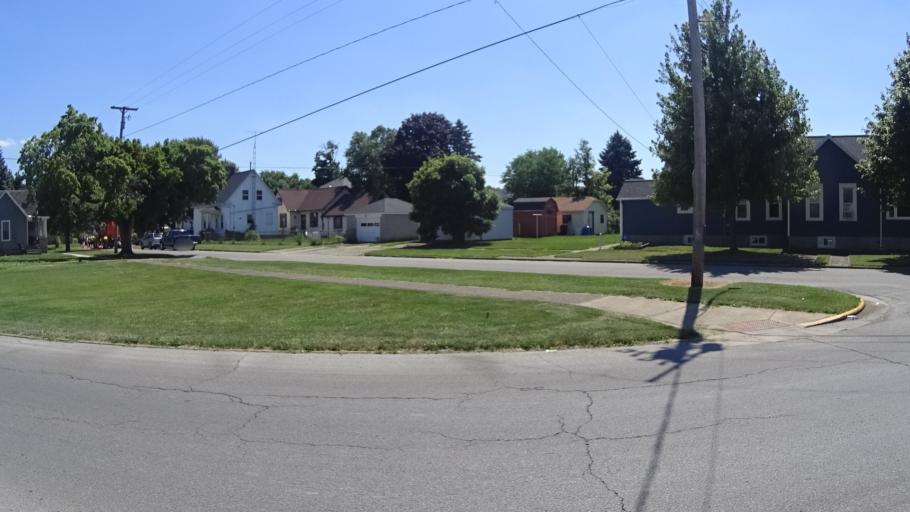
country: US
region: Ohio
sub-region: Erie County
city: Sandusky
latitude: 41.4475
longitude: -82.6987
